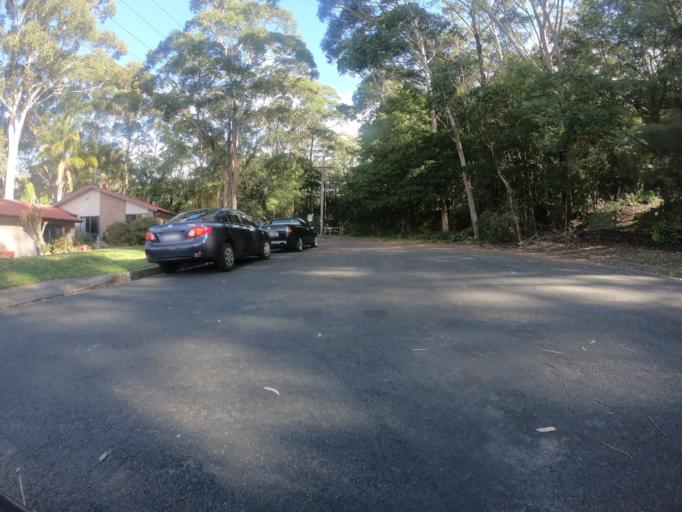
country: AU
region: New South Wales
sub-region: Wollongong
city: Bulli
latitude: -34.3058
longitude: 150.9211
